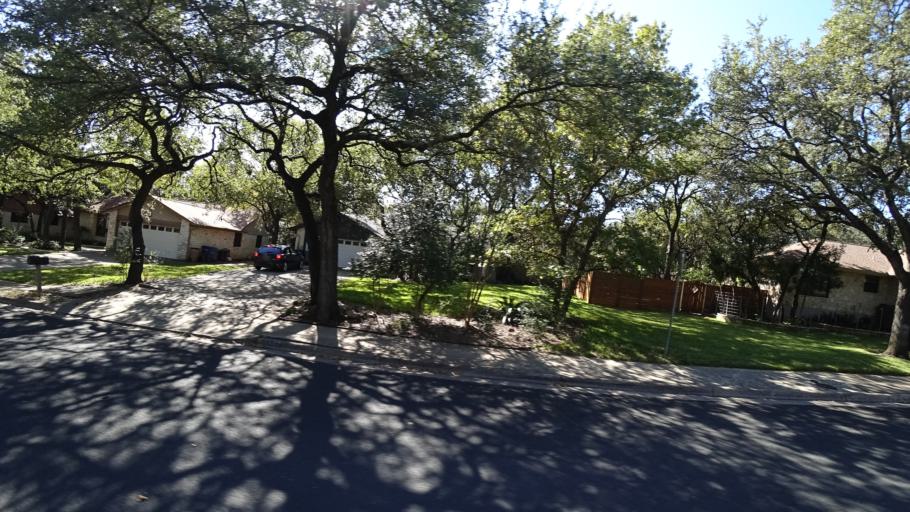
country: US
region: Texas
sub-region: Williamson County
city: Jollyville
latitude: 30.4192
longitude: -97.7673
